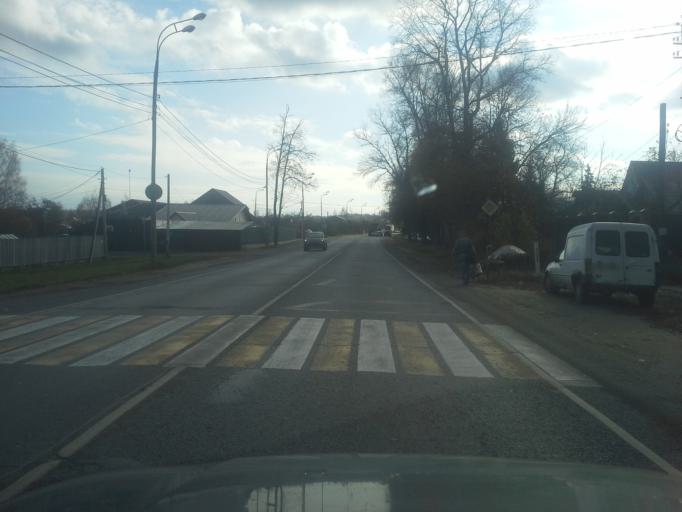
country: RU
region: Moskovskaya
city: Zvenigorod
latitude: 55.6961
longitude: 36.8883
